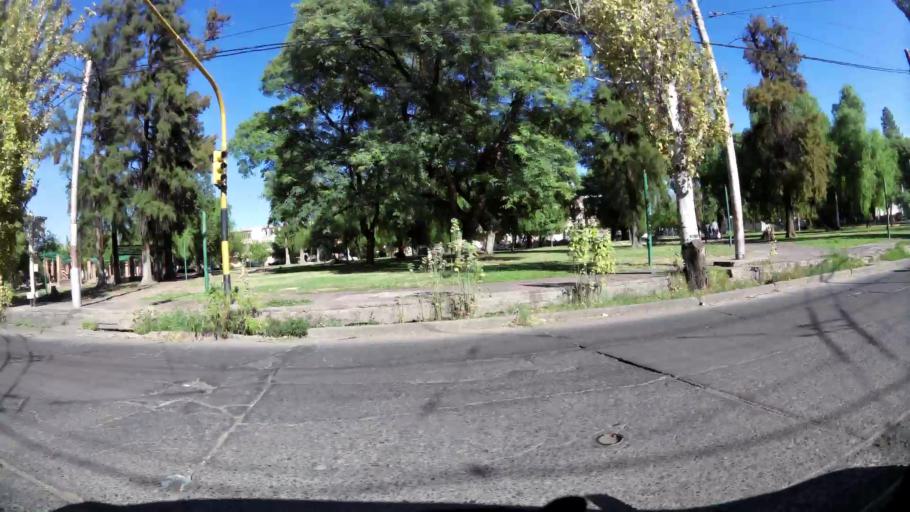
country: AR
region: Mendoza
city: Las Heras
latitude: -32.8692
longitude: -68.8581
